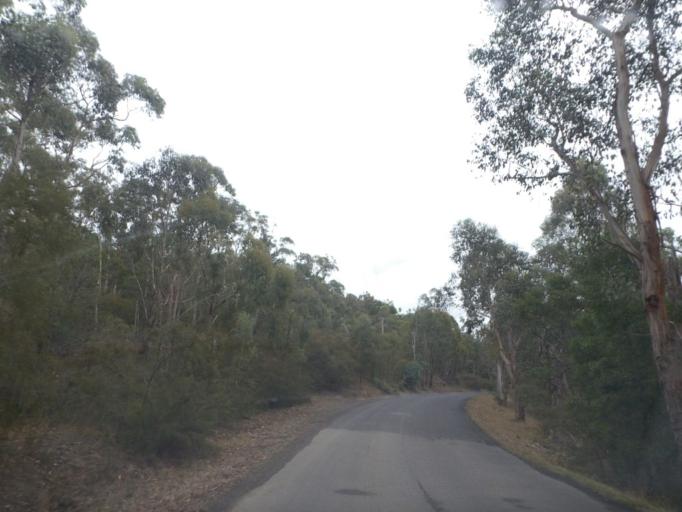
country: AU
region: Victoria
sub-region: Nillumbik
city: Saint Andrews
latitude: -37.5994
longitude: 145.2875
